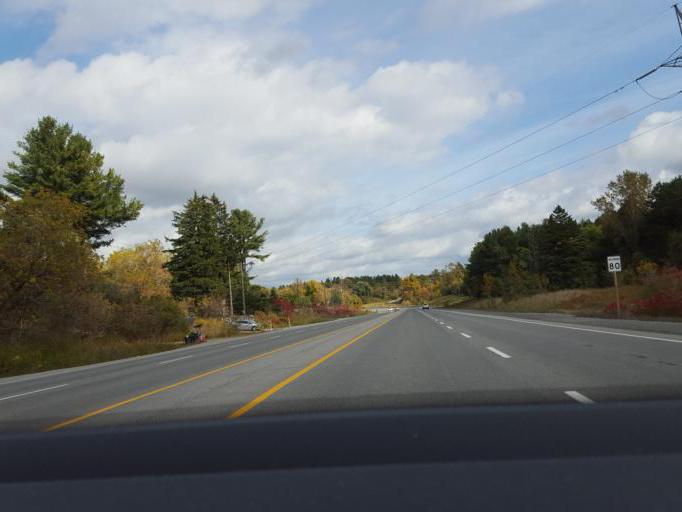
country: CA
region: Ontario
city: Pickering
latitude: 43.8807
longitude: -79.1046
